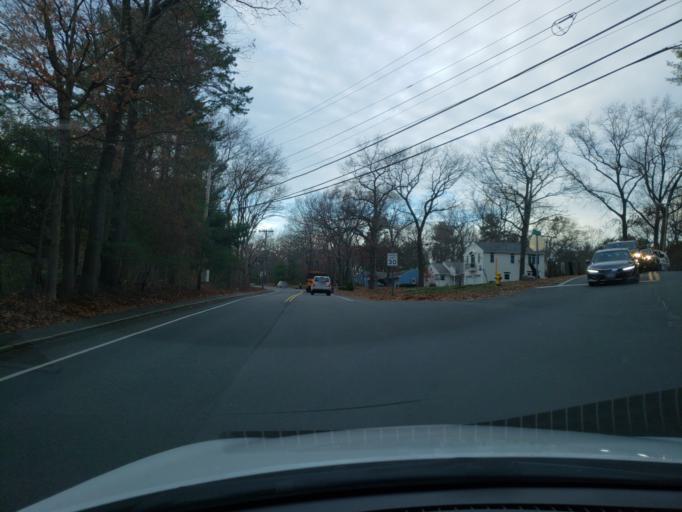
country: US
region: Massachusetts
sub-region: Essex County
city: Andover
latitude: 42.6682
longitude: -71.1736
